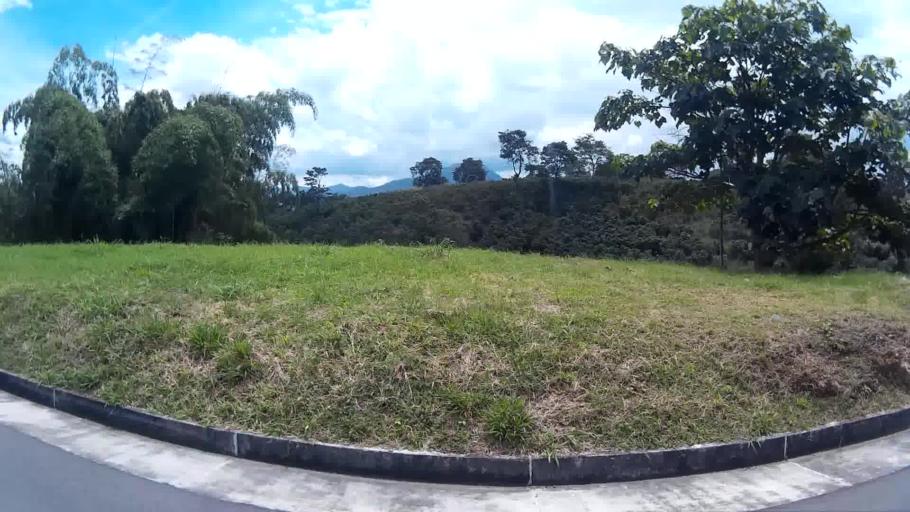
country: CO
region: Risaralda
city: Pereira
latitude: 4.7817
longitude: -75.7222
